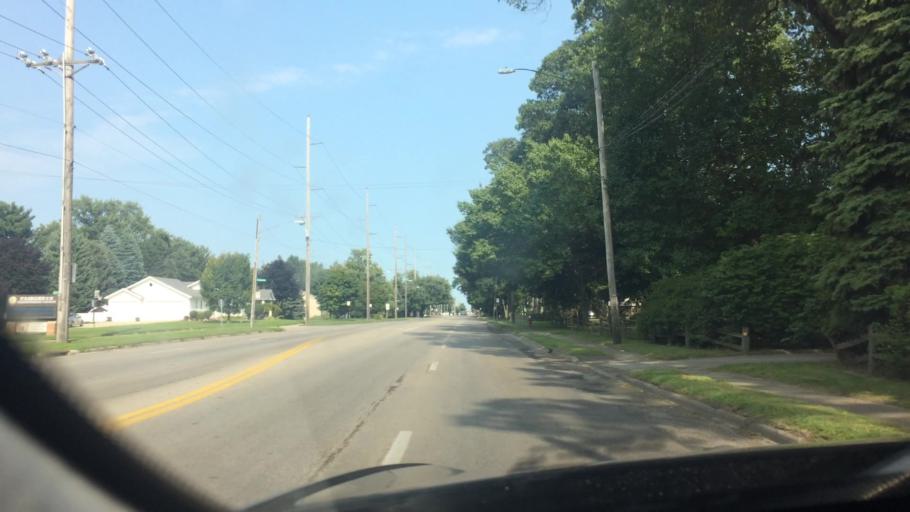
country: US
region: Ohio
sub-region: Lucas County
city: Ottawa Hills
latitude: 41.7063
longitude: -83.6222
